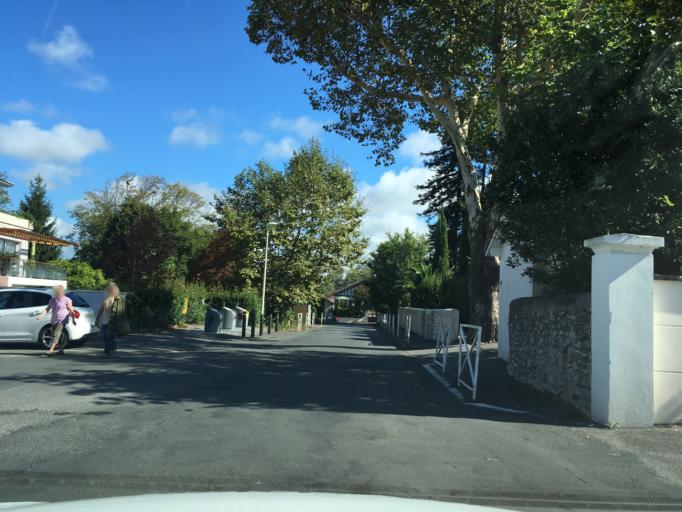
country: FR
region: Aquitaine
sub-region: Departement des Pyrenees-Atlantiques
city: Bayonne
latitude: 43.5052
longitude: -1.4759
